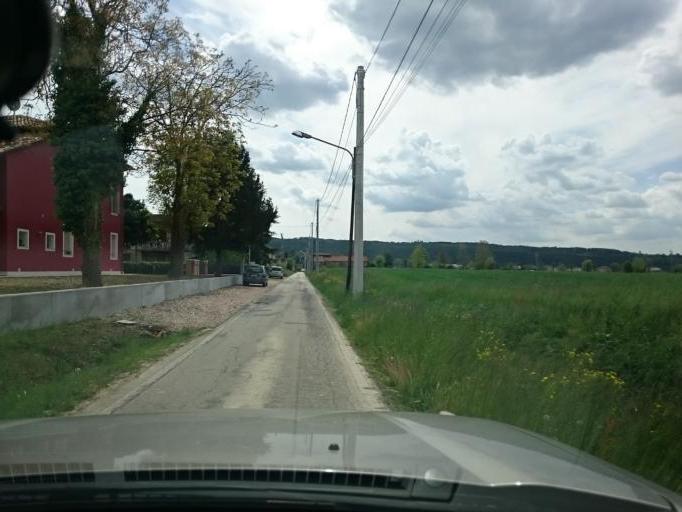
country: IT
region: Veneto
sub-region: Provincia di Vicenza
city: Longare
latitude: 45.5044
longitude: 11.5973
